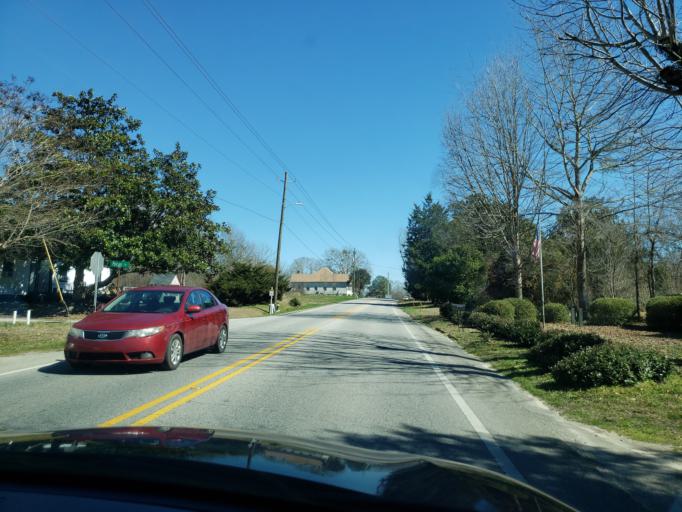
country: US
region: Alabama
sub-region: Lee County
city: Auburn
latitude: 32.6044
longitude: -85.5961
